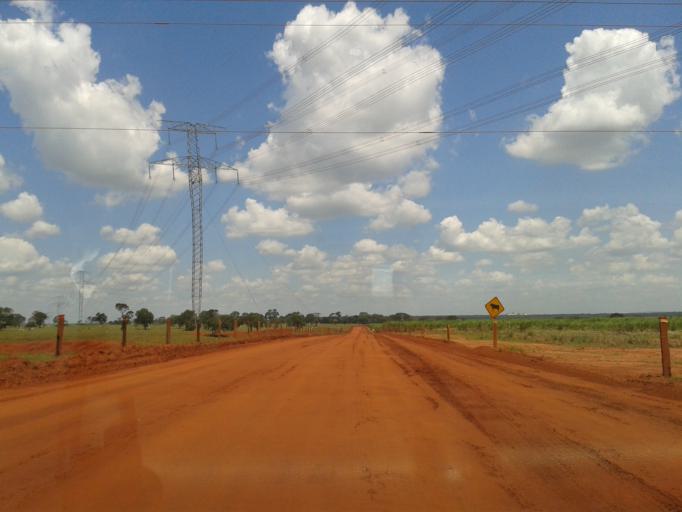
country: BR
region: Minas Gerais
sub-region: Ituiutaba
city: Ituiutaba
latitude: -18.9611
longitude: -49.6608
